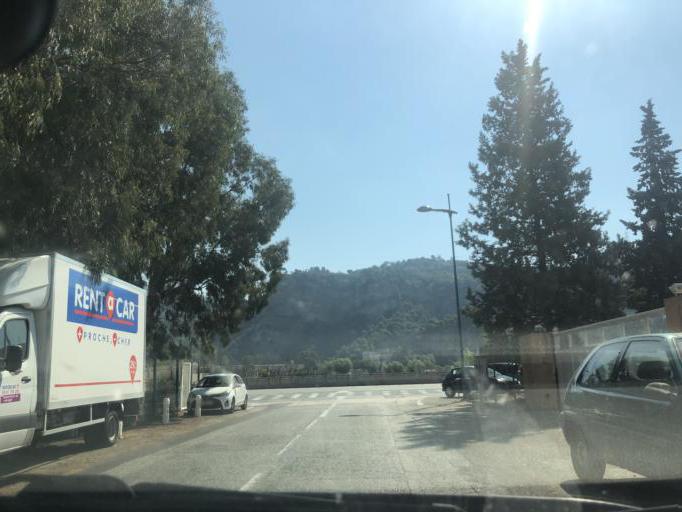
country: FR
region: Provence-Alpes-Cote d'Azur
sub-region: Departement des Alpes-Maritimes
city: Colomars
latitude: 43.7739
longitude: 7.2101
